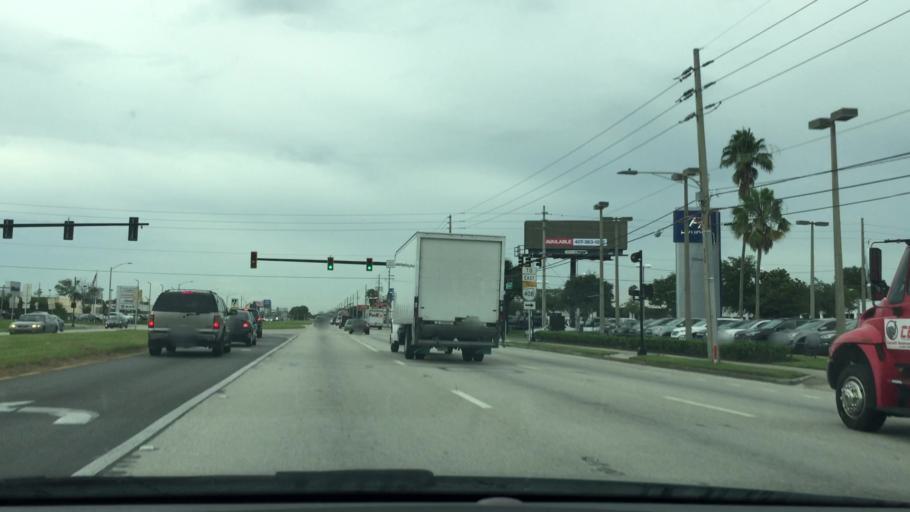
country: US
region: Florida
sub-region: Orange County
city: Pine Hills
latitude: 28.5526
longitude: -81.4312
